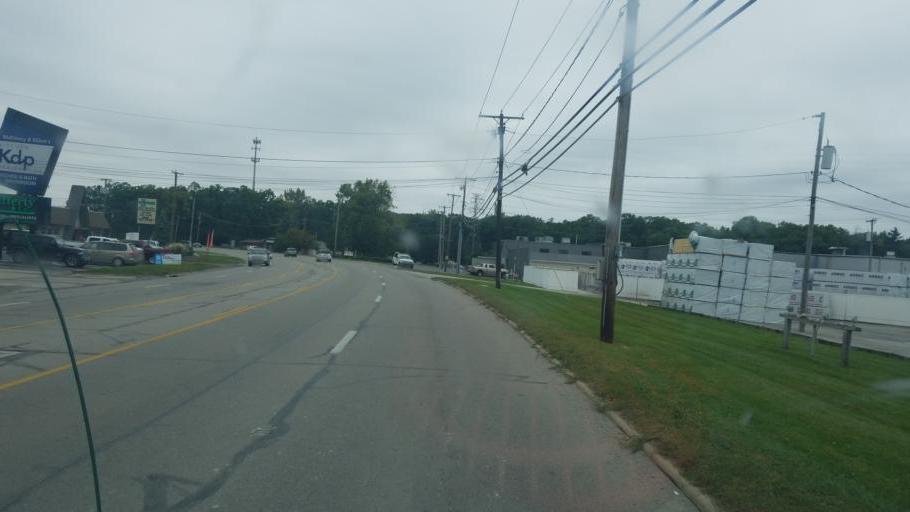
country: US
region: Ohio
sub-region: Lucas County
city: Ottawa Hills
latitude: 41.6711
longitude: -83.6681
